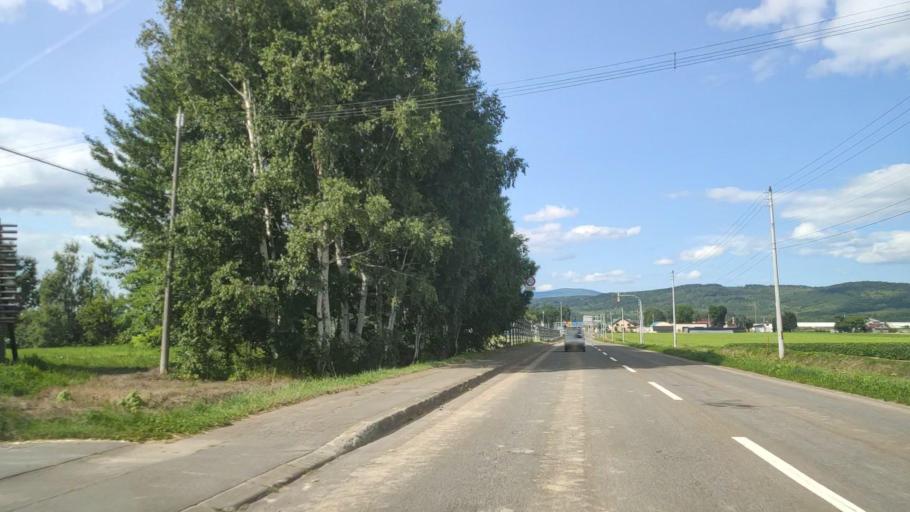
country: JP
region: Hokkaido
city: Nayoro
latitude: 44.4330
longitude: 142.4017
